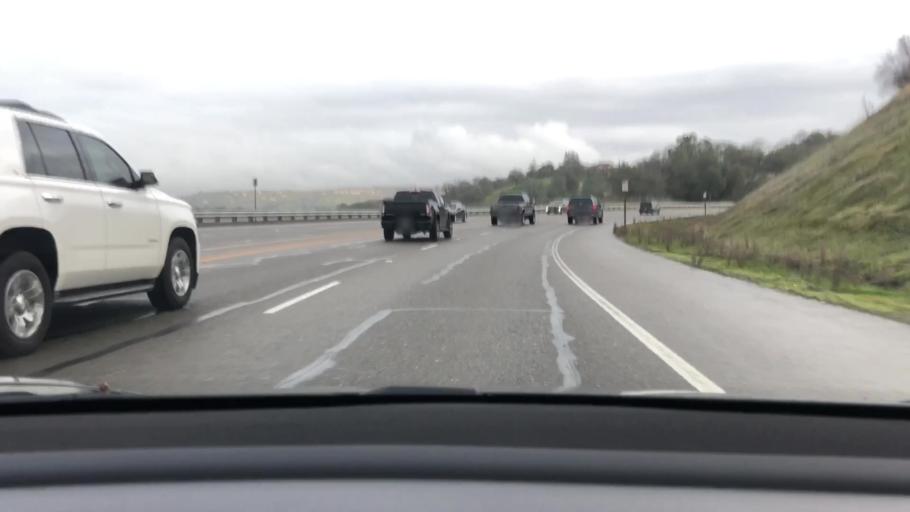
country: US
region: California
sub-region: Sacramento County
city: Folsom
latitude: 38.6998
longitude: -121.1450
